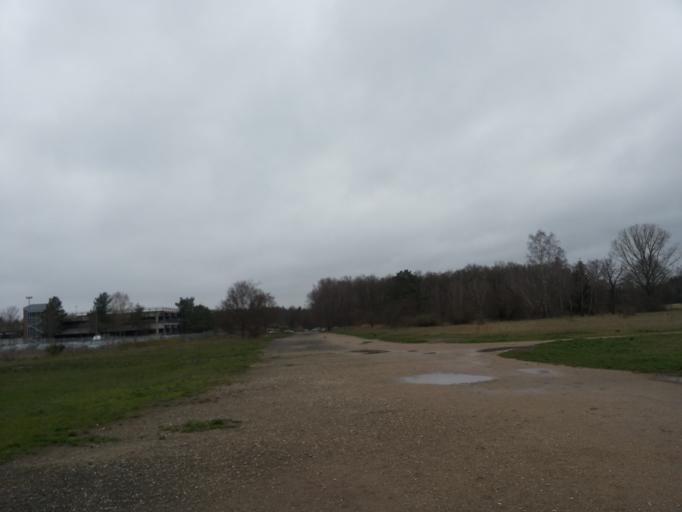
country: DE
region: Bavaria
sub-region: Regierungsbezirk Mittelfranken
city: Wendelstein
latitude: 49.4013
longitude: 11.1649
